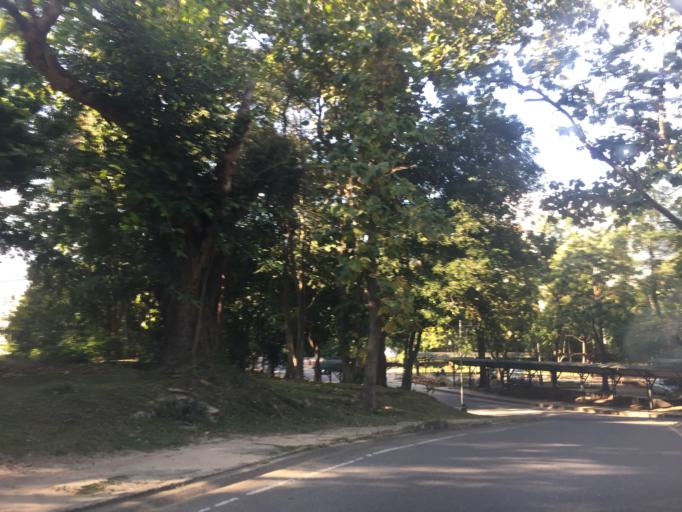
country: TH
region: Chiang Mai
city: Chiang Mai
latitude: 18.7994
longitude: 98.9519
